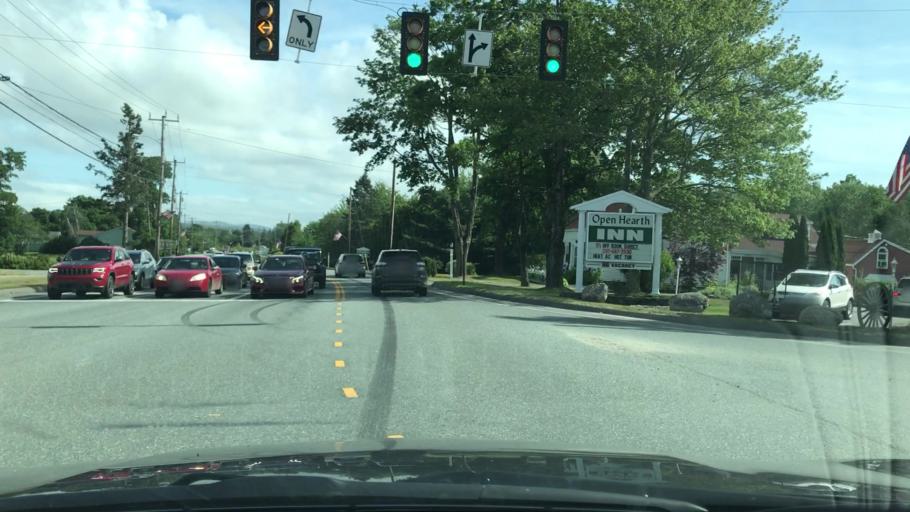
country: US
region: Maine
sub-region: Hancock County
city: Trenton
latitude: 44.4393
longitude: -68.3703
